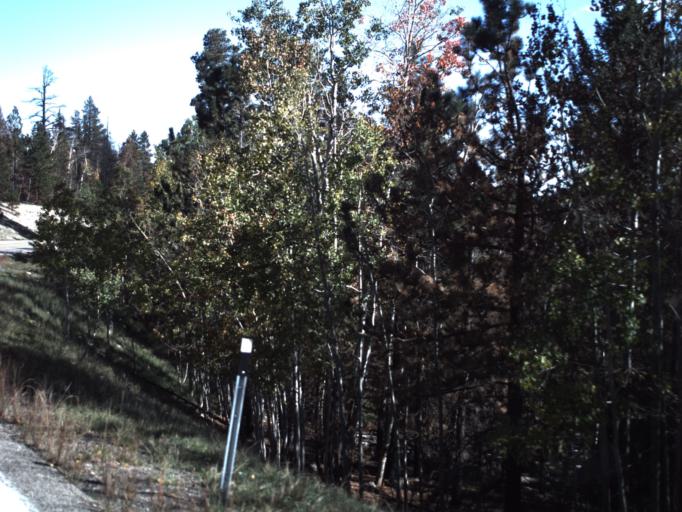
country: US
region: Utah
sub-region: Iron County
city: Parowan
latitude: 37.6545
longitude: -112.7023
